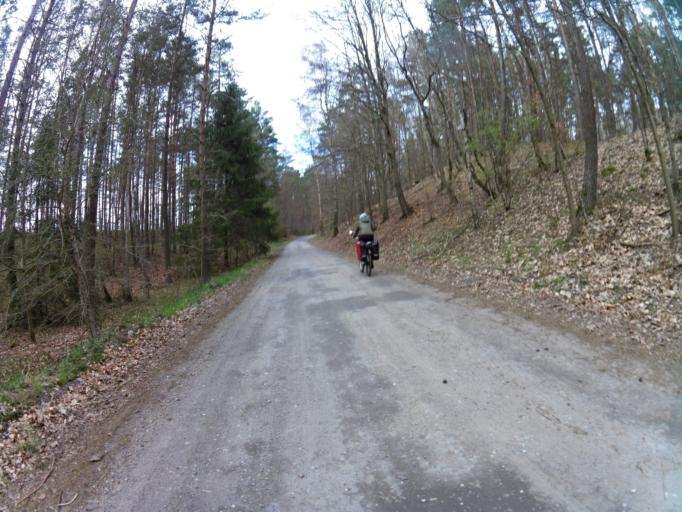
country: PL
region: West Pomeranian Voivodeship
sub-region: Powiat koszalinski
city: Bobolice
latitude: 53.8608
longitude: 16.6834
